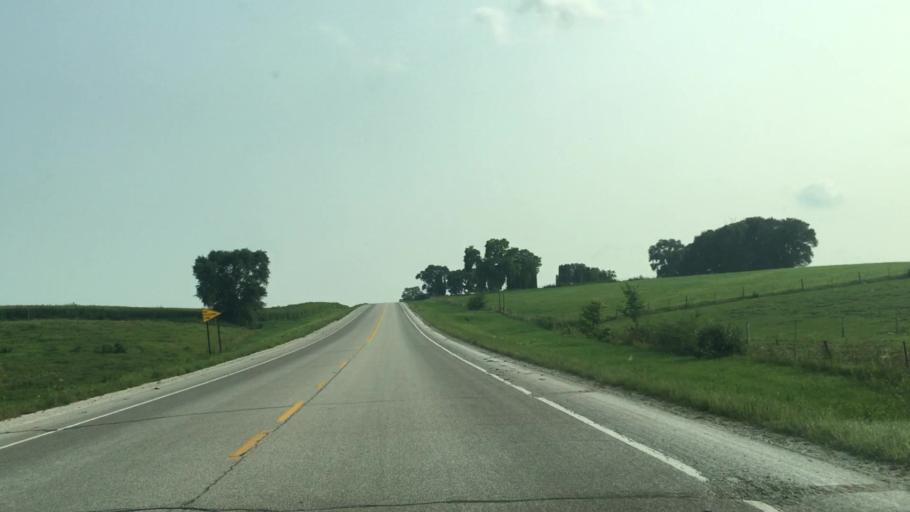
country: US
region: Minnesota
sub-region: Fillmore County
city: Harmony
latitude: 43.5429
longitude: -91.9296
